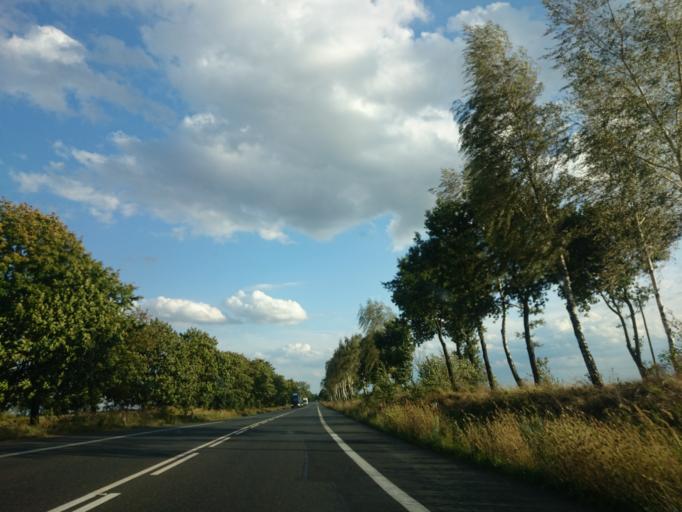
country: PL
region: West Pomeranian Voivodeship
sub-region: Powiat pyrzycki
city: Lipiany
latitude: 53.0351
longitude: 14.9274
